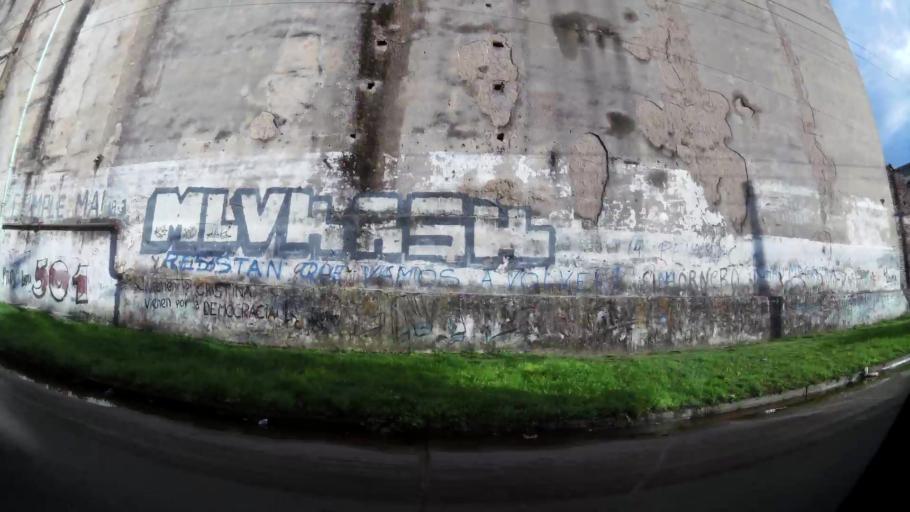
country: AR
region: Buenos Aires
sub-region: Partido de Lomas de Zamora
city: Lomas de Zamora
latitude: -34.7440
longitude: -58.3533
